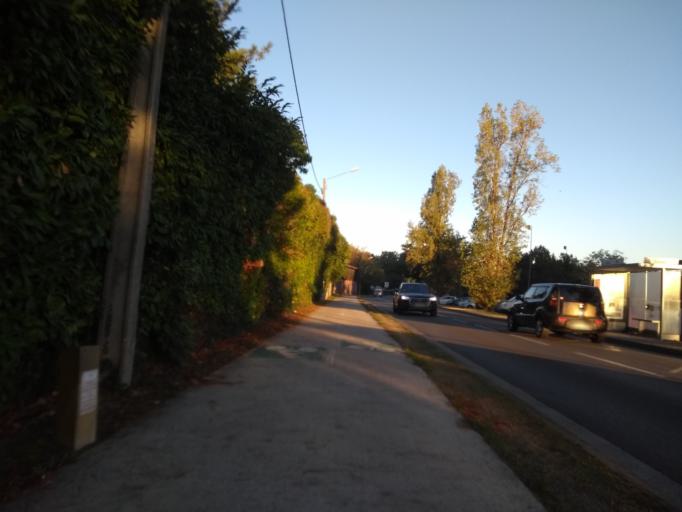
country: FR
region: Aquitaine
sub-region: Departement de la Gironde
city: Gradignan
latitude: 44.7880
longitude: -0.6114
